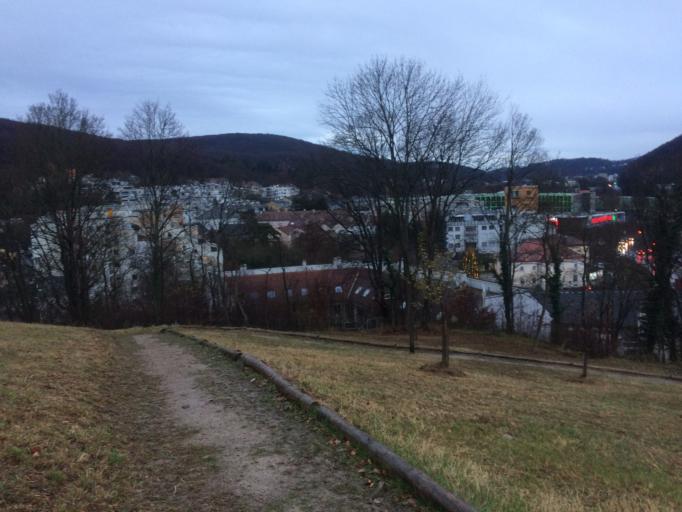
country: AT
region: Lower Austria
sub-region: Politischer Bezirk Wien-Umgebung
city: Purkersdorf
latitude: 48.2084
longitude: 16.1746
